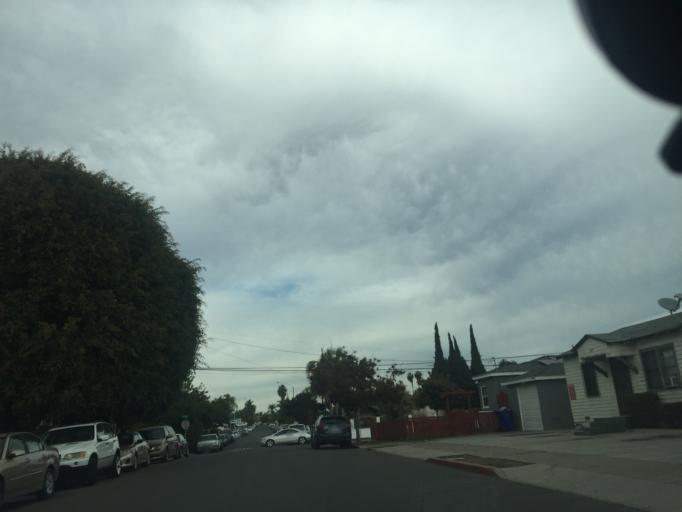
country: US
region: California
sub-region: San Diego County
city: Lemon Grove
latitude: 32.7548
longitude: -117.0901
